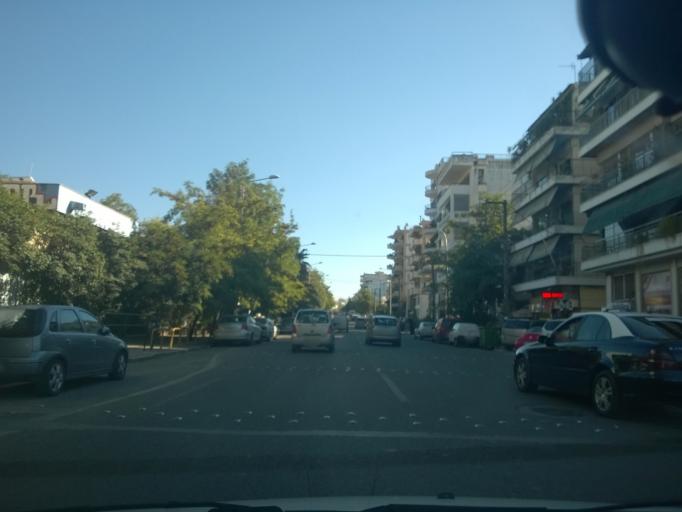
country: GR
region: Central Macedonia
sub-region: Nomos Thessalonikis
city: Kalamaria
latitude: 40.5950
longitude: 22.9538
